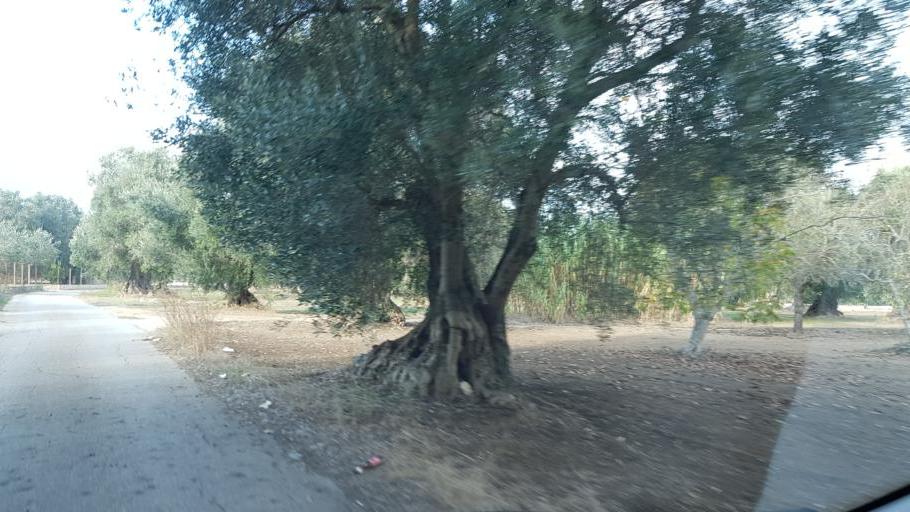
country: IT
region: Apulia
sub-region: Provincia di Brindisi
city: Oria
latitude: 40.5068
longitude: 17.6715
